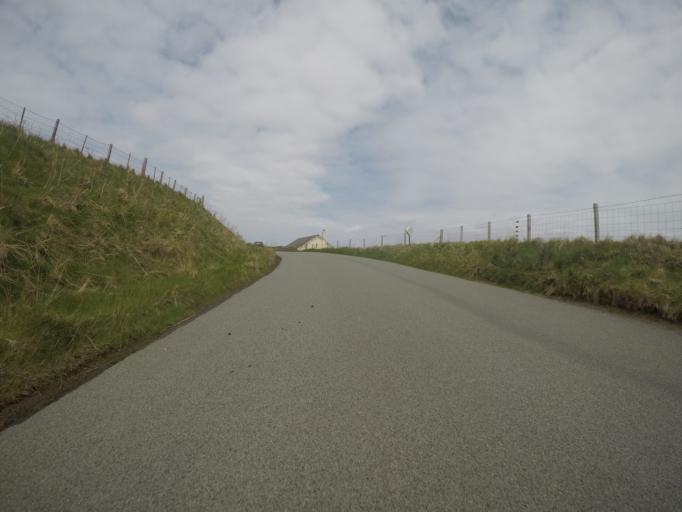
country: GB
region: Scotland
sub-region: Highland
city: Portree
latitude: 57.6353
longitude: -6.2404
